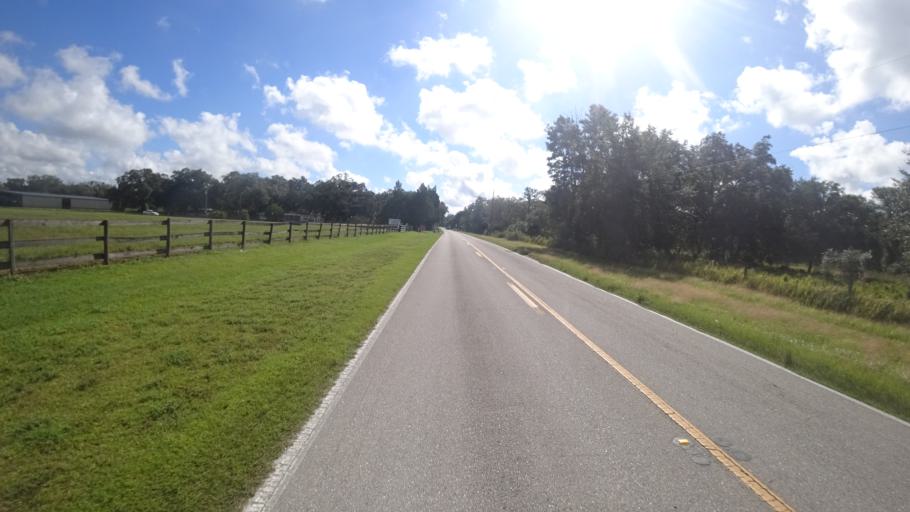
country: US
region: Florida
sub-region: Sarasota County
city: Lake Sarasota
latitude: 27.3420
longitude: -82.2083
